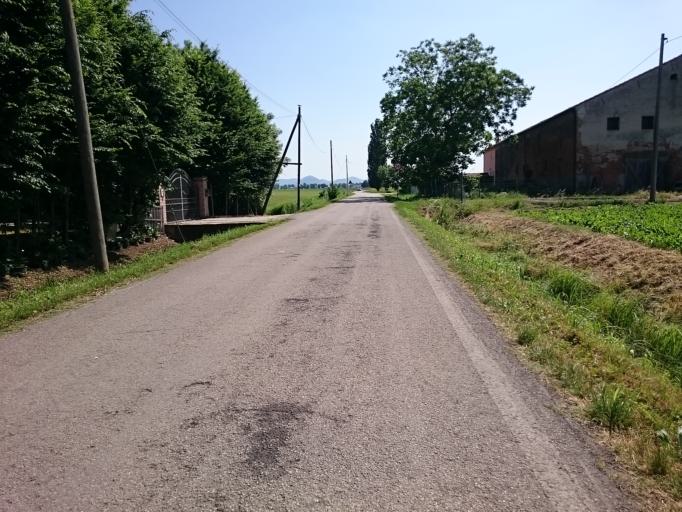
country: IT
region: Veneto
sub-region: Provincia di Padova
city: Megliadino San Fidenzio
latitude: 45.2451
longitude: 11.5057
